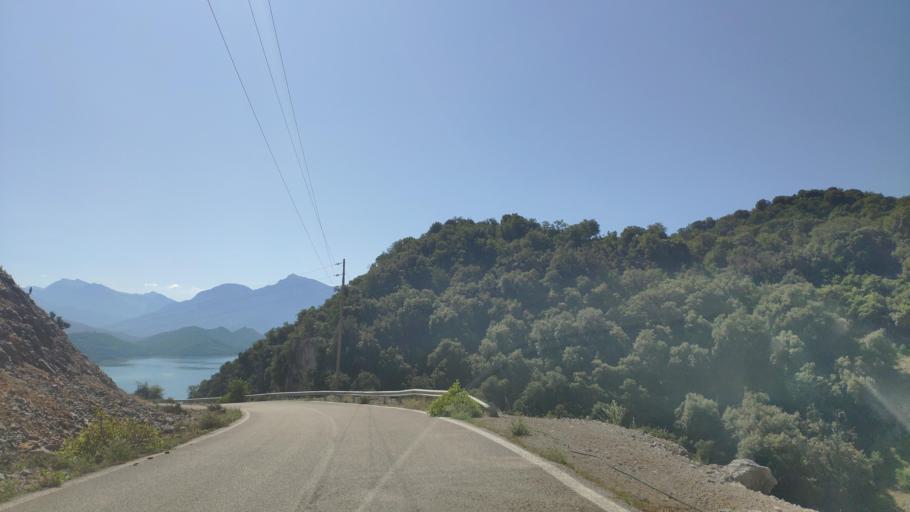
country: GR
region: Central Greece
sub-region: Nomos Evrytanias
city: Kerasochori
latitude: 38.9662
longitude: 21.4686
